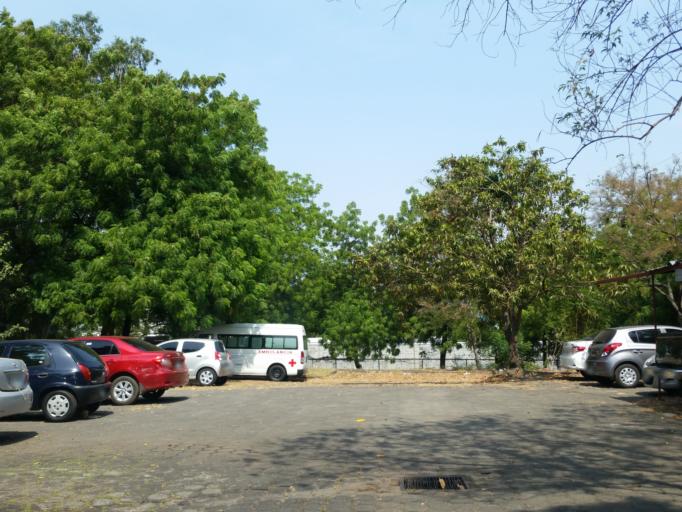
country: NI
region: Managua
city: Managua
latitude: 12.1249
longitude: -86.2989
